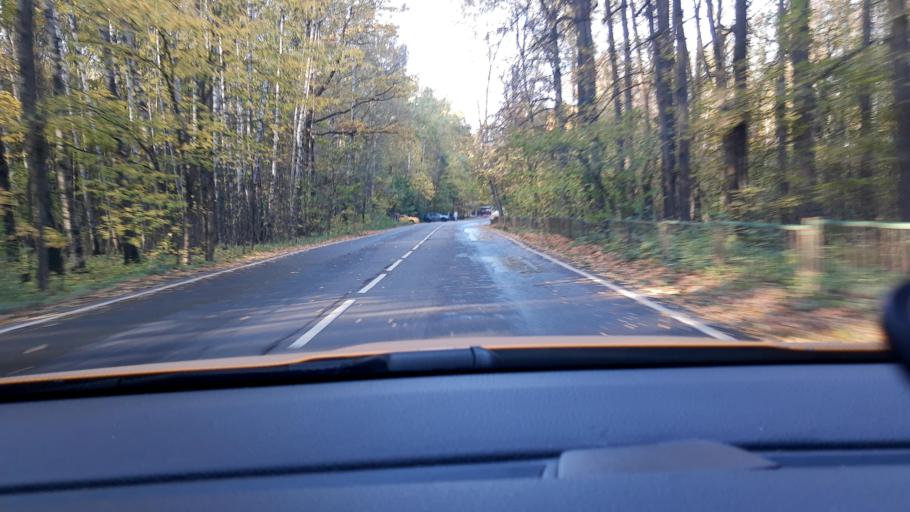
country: RU
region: Moskovskaya
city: Bogorodskoye
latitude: 55.8318
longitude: 37.7452
